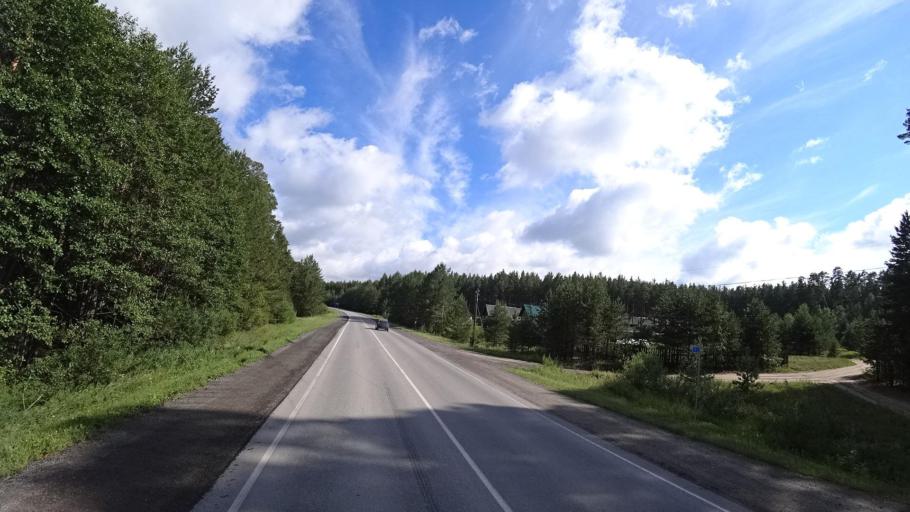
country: RU
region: Sverdlovsk
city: Kamyshlov
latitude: 56.8298
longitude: 62.6957
